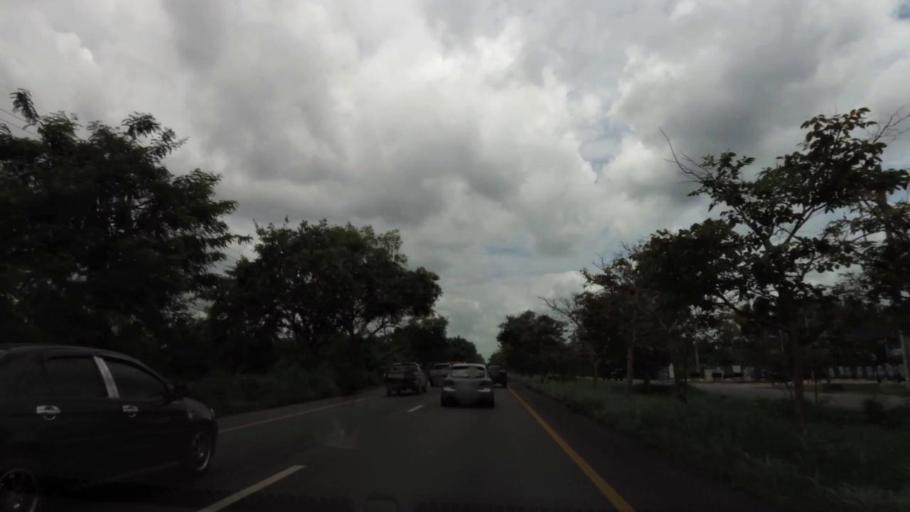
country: TH
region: Rayong
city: Klaeng
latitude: 12.7841
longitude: 101.6856
